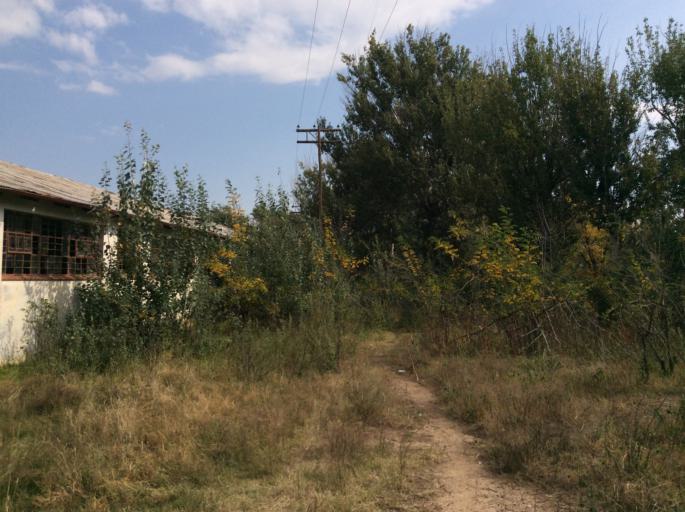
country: LS
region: Mafeteng
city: Mafeteng
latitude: -29.7264
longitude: 27.0399
